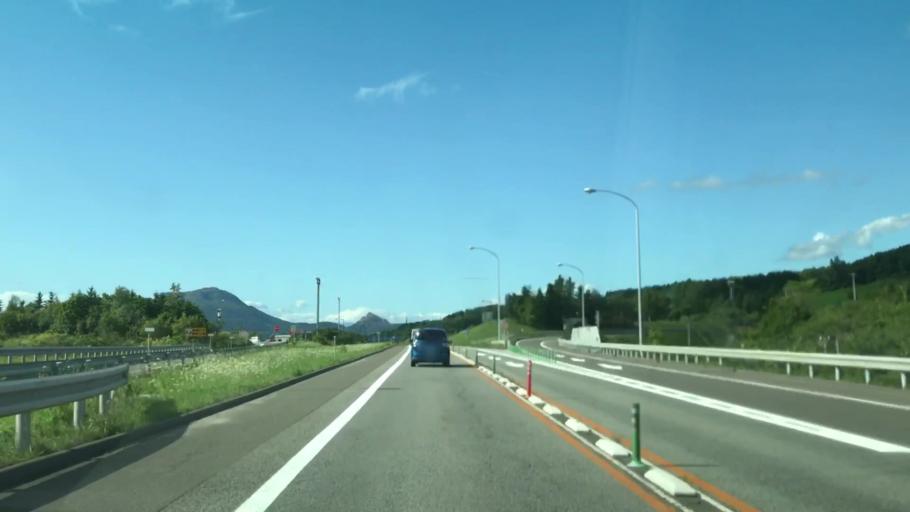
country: JP
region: Hokkaido
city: Date
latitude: 42.4637
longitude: 140.9100
